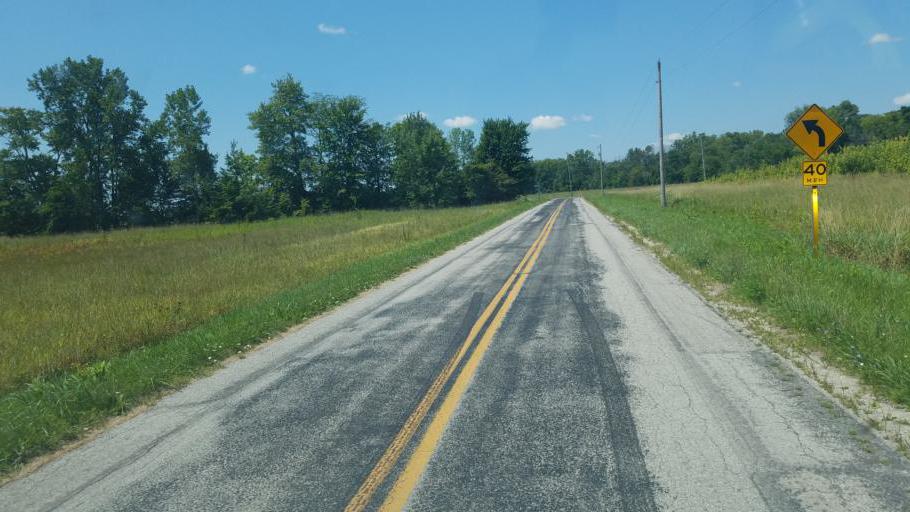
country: US
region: Ohio
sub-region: Union County
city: Richwood
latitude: 40.5623
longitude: -83.3134
